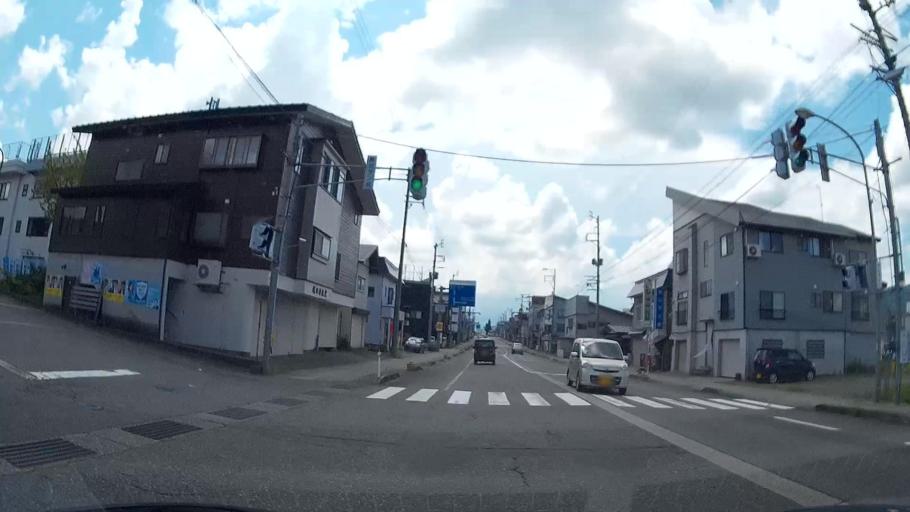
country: JP
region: Niigata
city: Tokamachi
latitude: 37.0539
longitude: 138.6990
